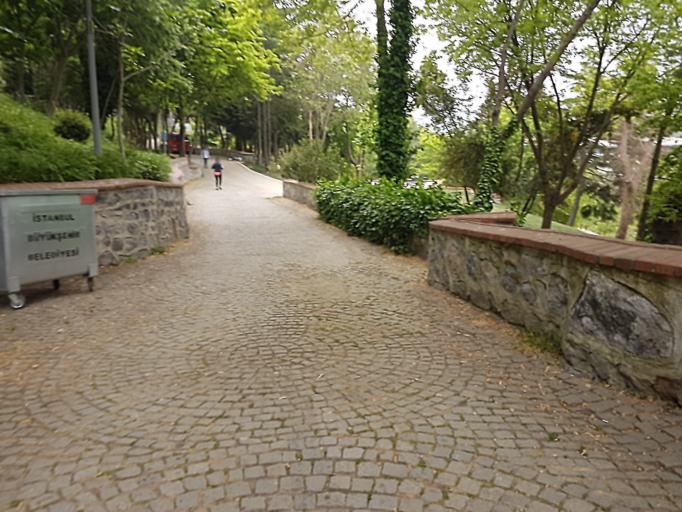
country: TR
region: Istanbul
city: Sisli
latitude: 41.0440
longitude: 28.9942
